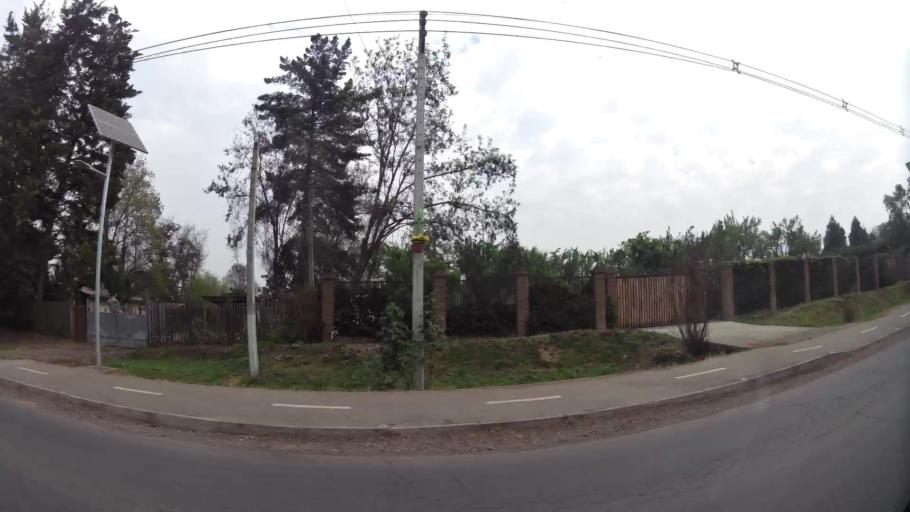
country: CL
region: Santiago Metropolitan
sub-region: Provincia de Chacabuco
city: Chicureo Abajo
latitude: -33.1972
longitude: -70.6784
